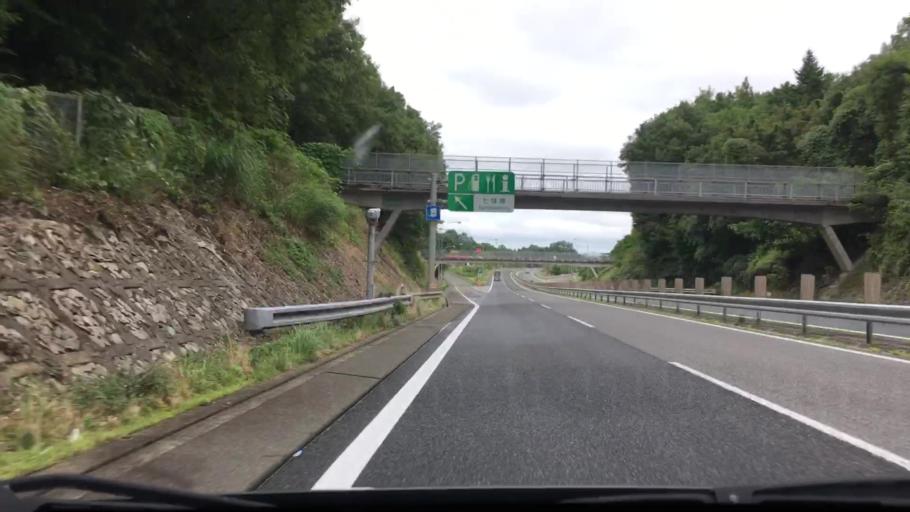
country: JP
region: Hiroshima
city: Shobara
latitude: 34.8298
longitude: 132.9628
